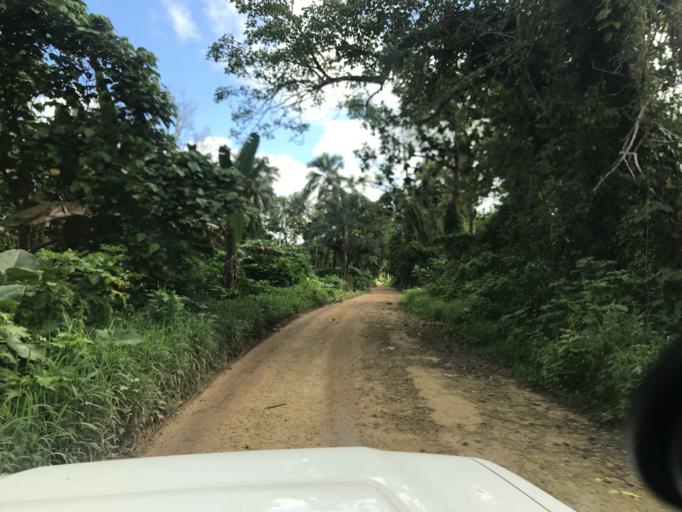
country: VU
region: Sanma
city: Luganville
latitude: -15.4782
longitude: 167.0874
